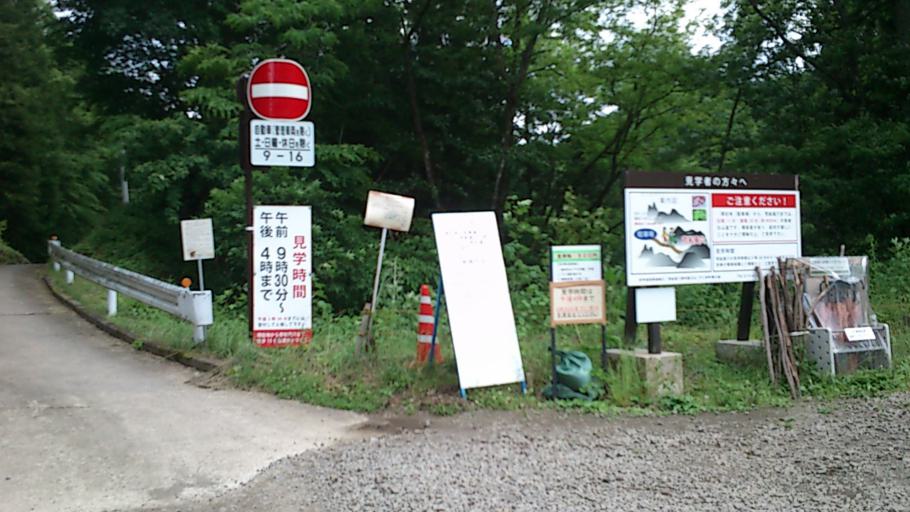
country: JP
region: Nagano
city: Saku
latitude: 36.2475
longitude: 138.6304
